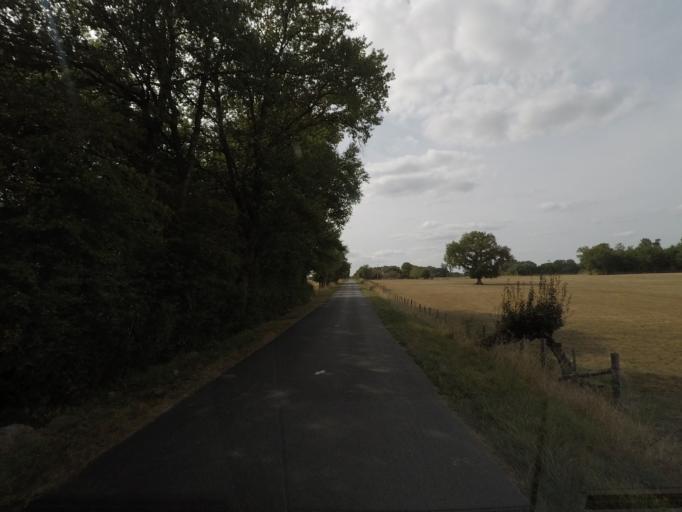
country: FR
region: Poitou-Charentes
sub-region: Departement de la Charente
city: Loubert
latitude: 45.9420
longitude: 0.5203
